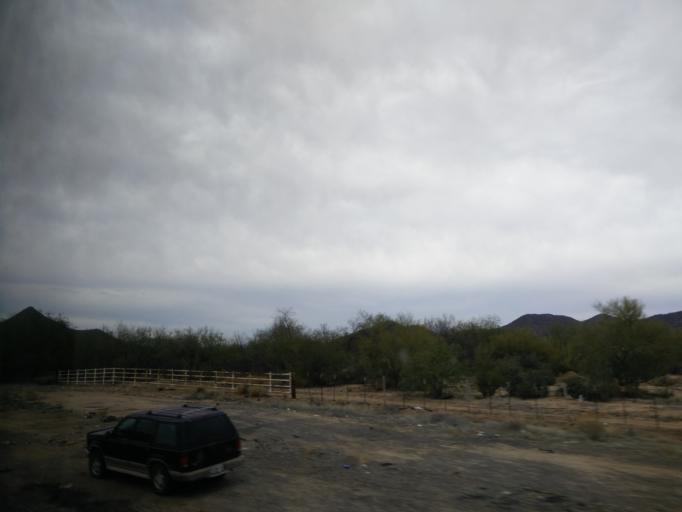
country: MX
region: Sonora
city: Hermosillo
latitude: 28.7929
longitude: -110.9607
